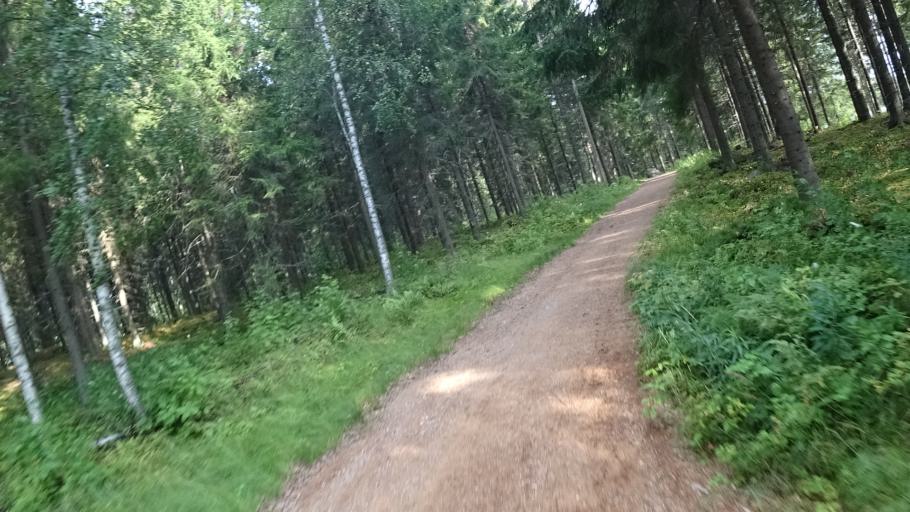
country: FI
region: North Karelia
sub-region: Joensuu
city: Ilomantsi
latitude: 62.6680
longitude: 30.9079
